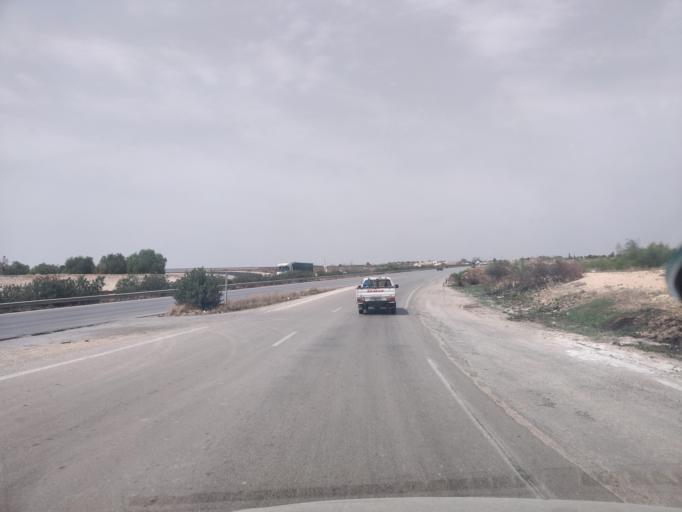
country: TN
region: Susah
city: Akouda
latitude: 35.8405
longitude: 10.5337
